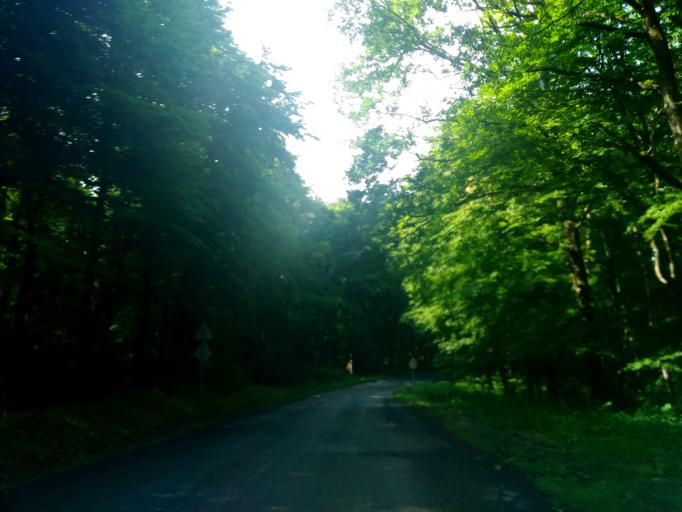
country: HU
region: Baranya
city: Pecs
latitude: 46.1242
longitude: 18.2170
